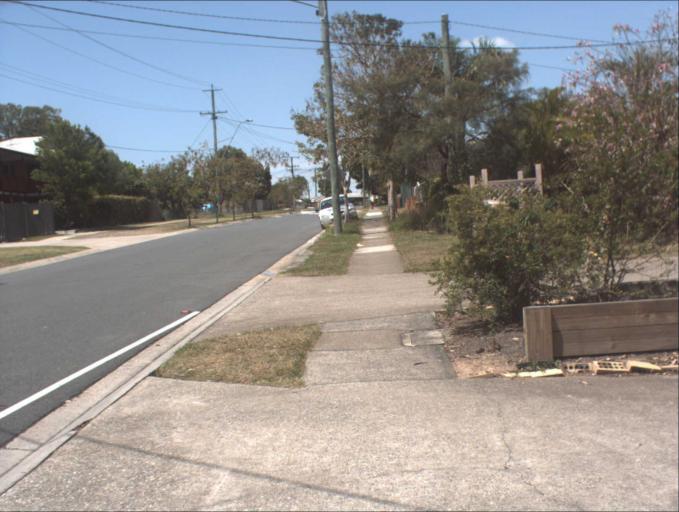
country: AU
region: Queensland
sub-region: Logan
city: Woodridge
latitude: -27.6395
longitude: 153.1001
